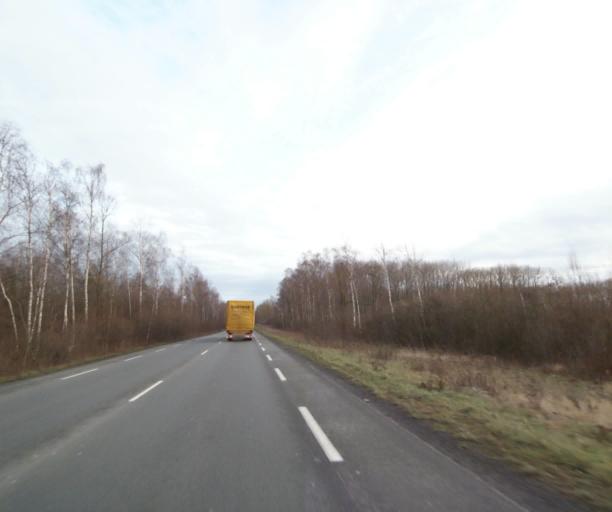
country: FR
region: Nord-Pas-de-Calais
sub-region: Departement du Nord
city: Escautpont
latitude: 50.3986
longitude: 3.5721
